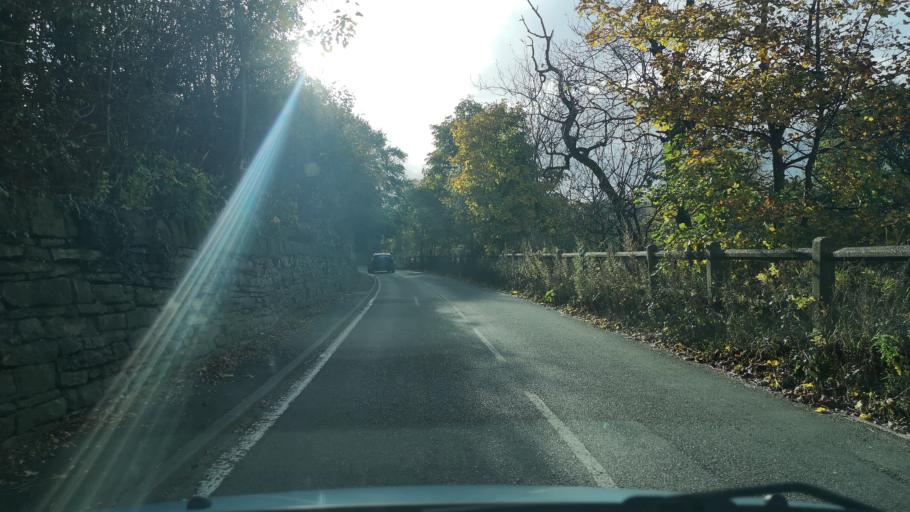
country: GB
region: England
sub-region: Kirklees
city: Mirfield
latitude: 53.6698
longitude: -1.6786
